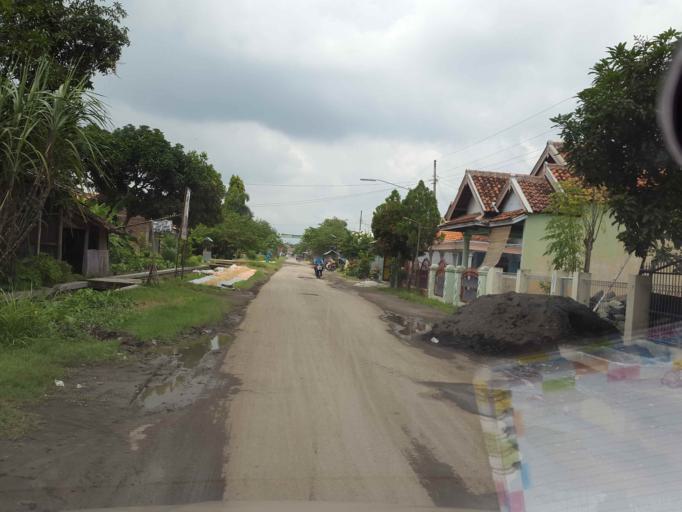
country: ID
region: Central Java
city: Bulakamba
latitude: -6.9554
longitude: 108.9930
